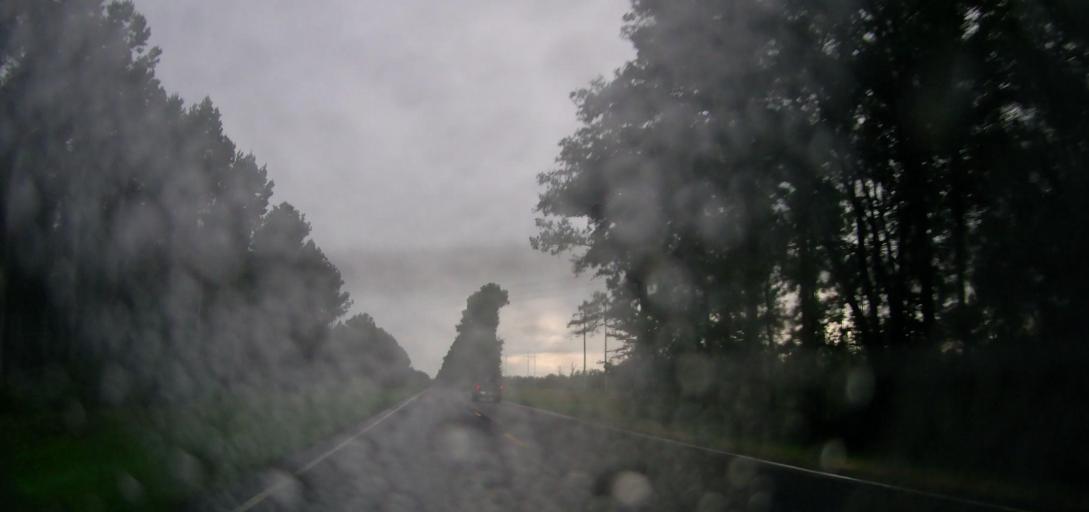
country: US
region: Georgia
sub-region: Glynn County
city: Dock Junction
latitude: 31.2742
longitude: -81.6507
